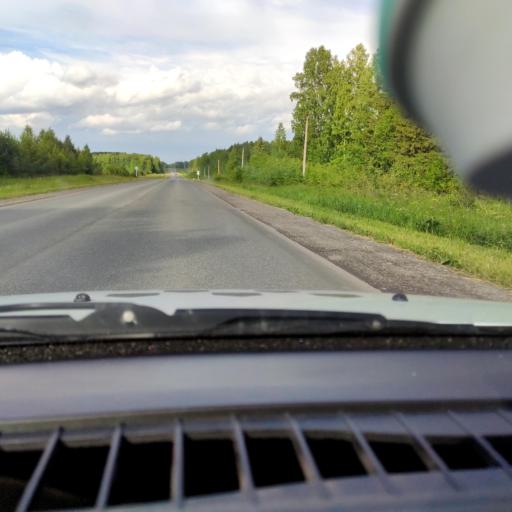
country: RU
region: Perm
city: Orda
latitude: 57.2350
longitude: 56.9758
